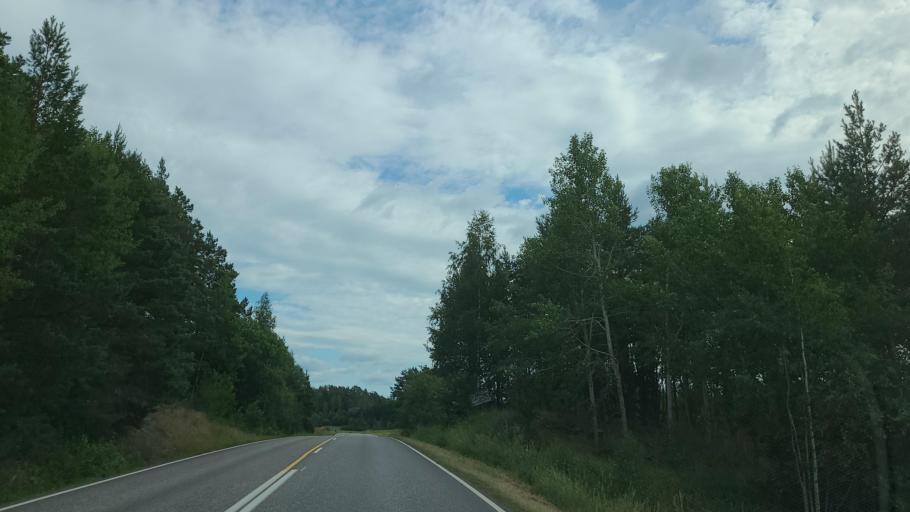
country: FI
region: Varsinais-Suomi
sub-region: Turku
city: Rymaettylae
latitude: 60.3569
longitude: 21.9525
